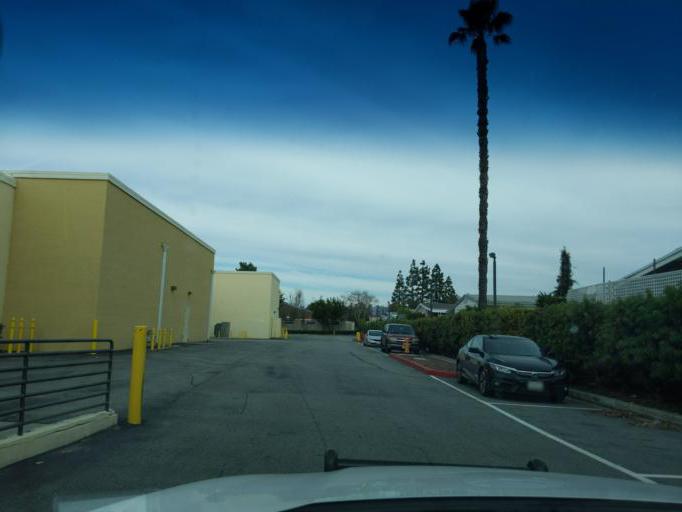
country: US
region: California
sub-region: Orange County
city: Laguna Hills
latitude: 33.6182
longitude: -117.7004
